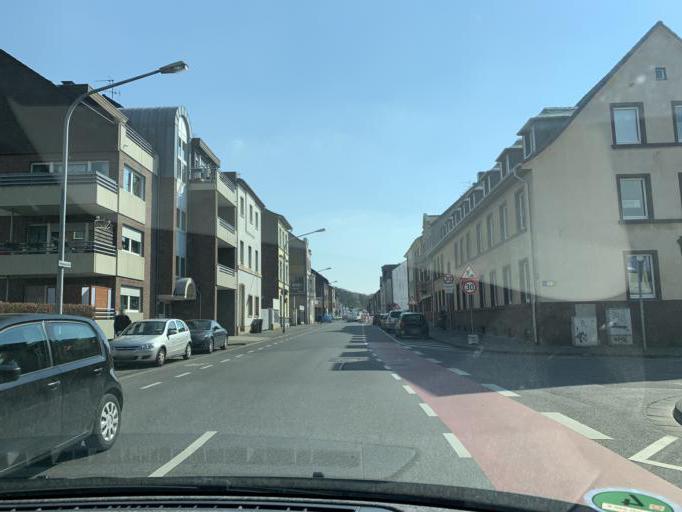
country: DE
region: North Rhine-Westphalia
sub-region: Regierungsbezirk Dusseldorf
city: Monchengladbach
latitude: 51.1471
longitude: 6.4565
